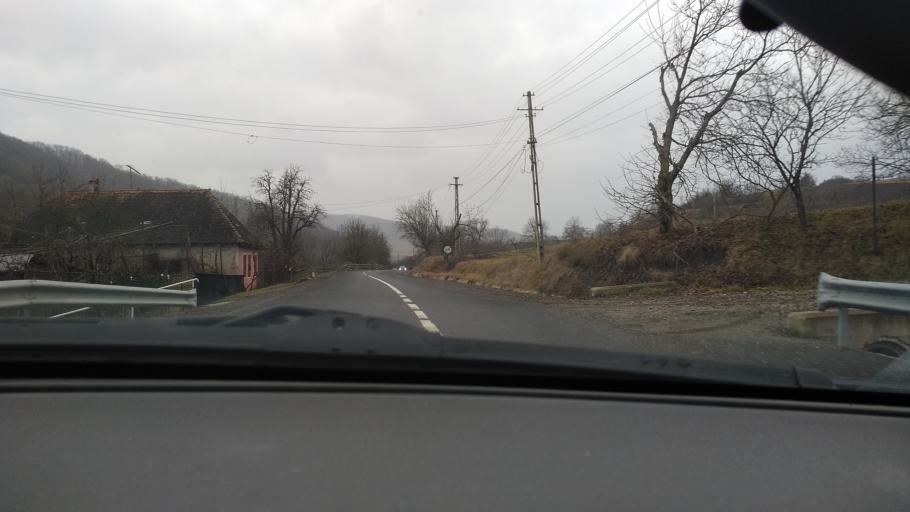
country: RO
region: Mures
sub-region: Comuna Magherani
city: Magherani
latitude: 46.5728
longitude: 24.9238
